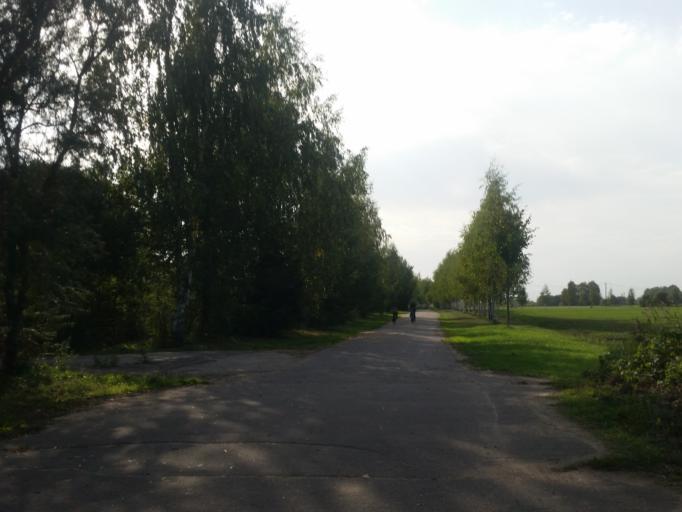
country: LV
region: Ikskile
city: Ikskile
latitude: 56.8178
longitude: 24.5507
